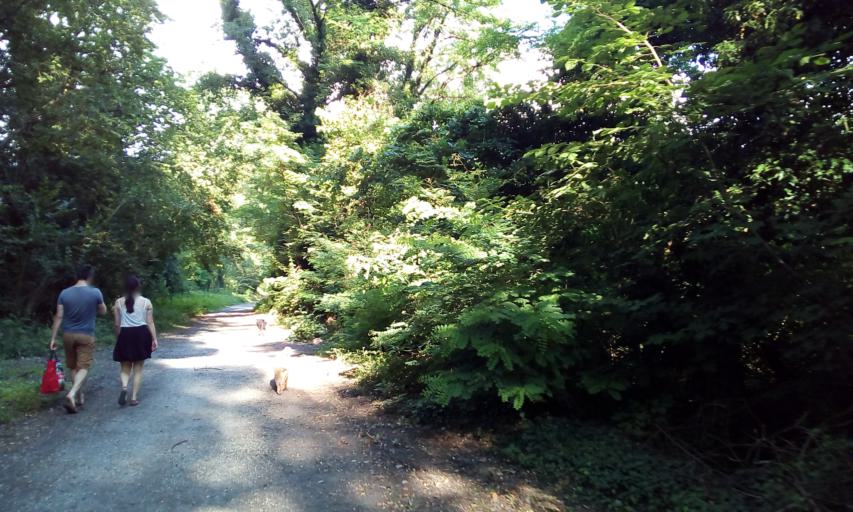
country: FR
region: Rhone-Alpes
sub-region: Departement de l'Isere
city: Gieres
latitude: 45.1923
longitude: 5.7964
